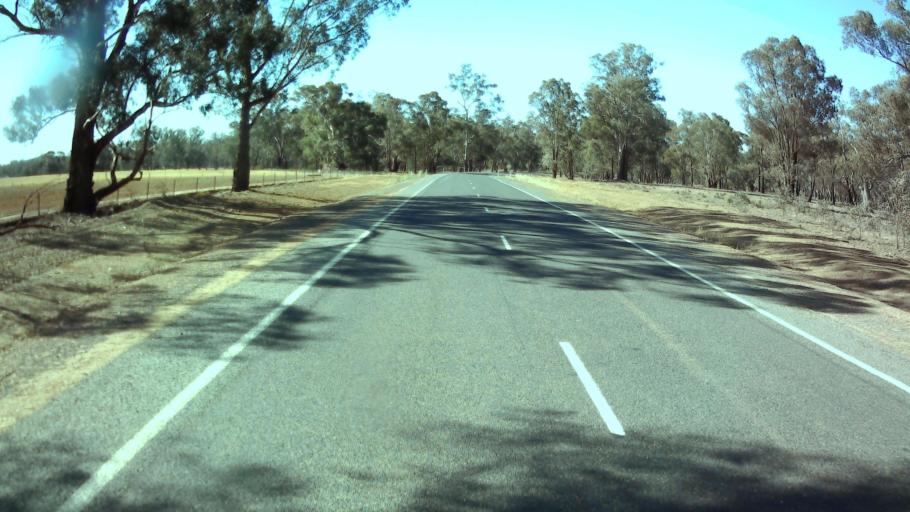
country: AU
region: New South Wales
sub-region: Weddin
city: Grenfell
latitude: -33.7654
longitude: 148.0823
